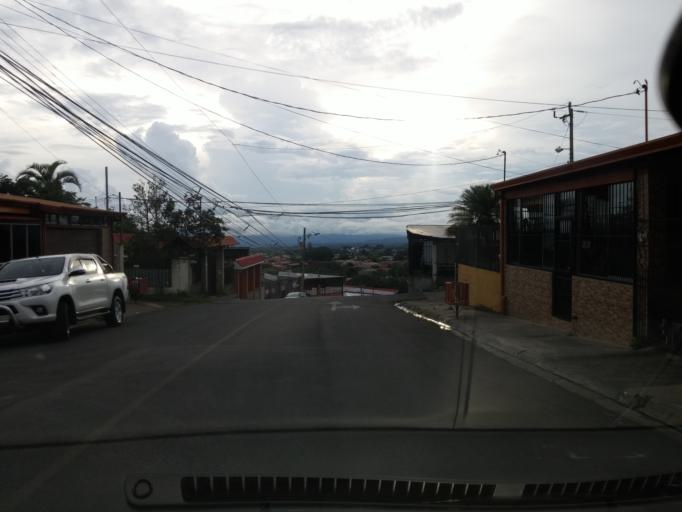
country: CR
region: Heredia
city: San Rafael
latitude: 10.0134
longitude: -84.1096
